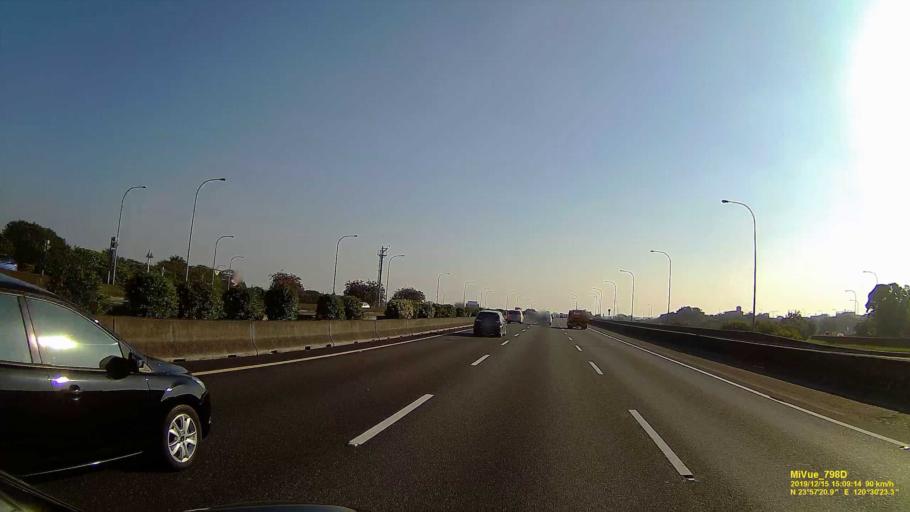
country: TW
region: Taiwan
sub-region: Changhua
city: Chang-hua
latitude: 23.9553
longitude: 120.5065
